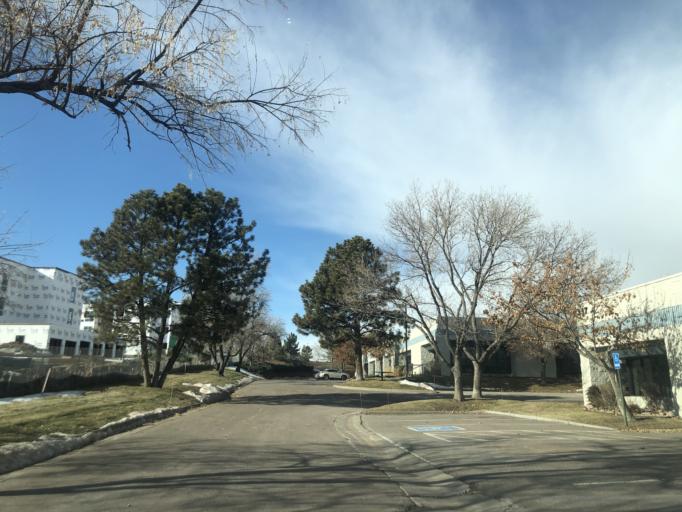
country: US
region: Colorado
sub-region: Douglas County
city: Meridian
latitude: 39.5584
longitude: -104.8630
